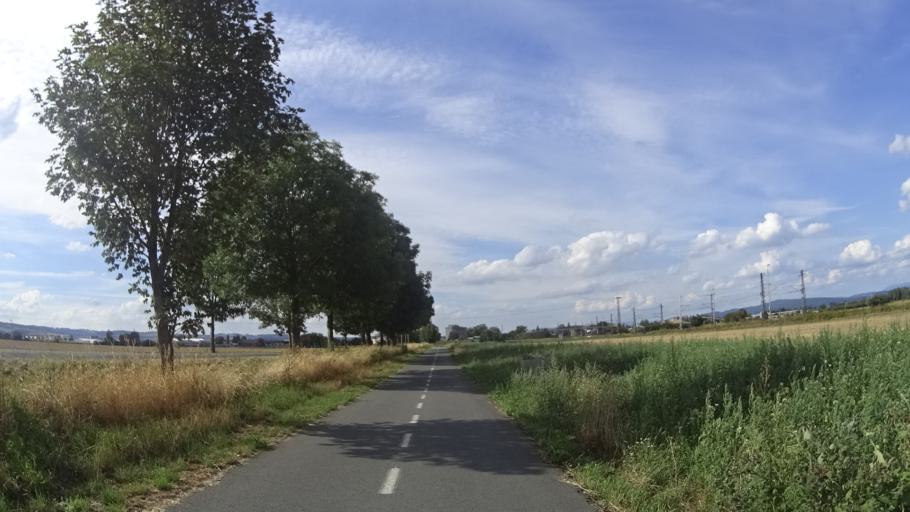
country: CZ
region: Olomoucky
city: Moravicany
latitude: 49.7661
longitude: 16.9484
